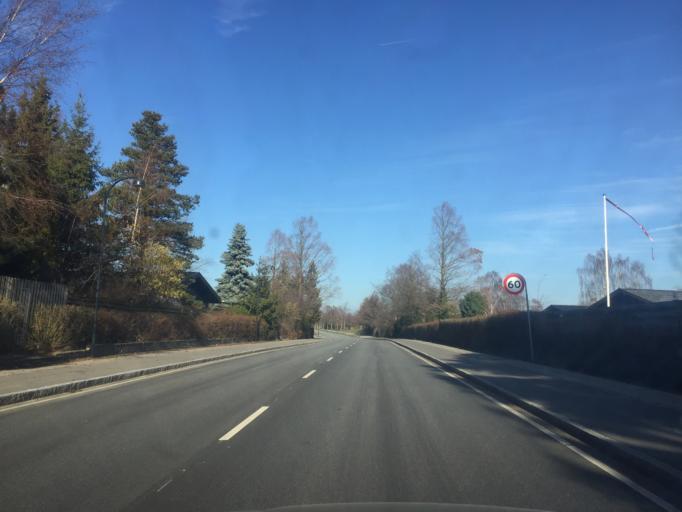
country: DK
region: Capital Region
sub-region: Rudersdal Kommune
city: Trorod
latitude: 55.8406
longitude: 12.5299
